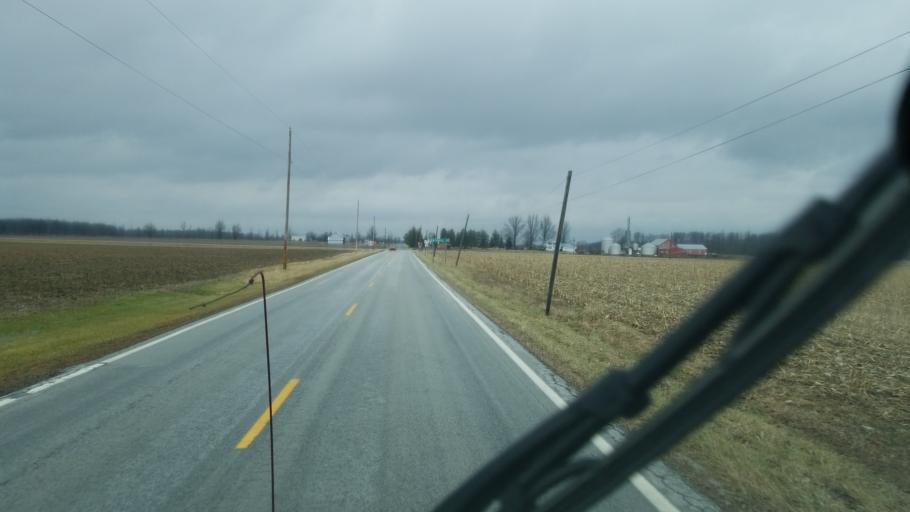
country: US
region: Ohio
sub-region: Hardin County
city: Forest
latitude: 40.8297
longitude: -83.4191
